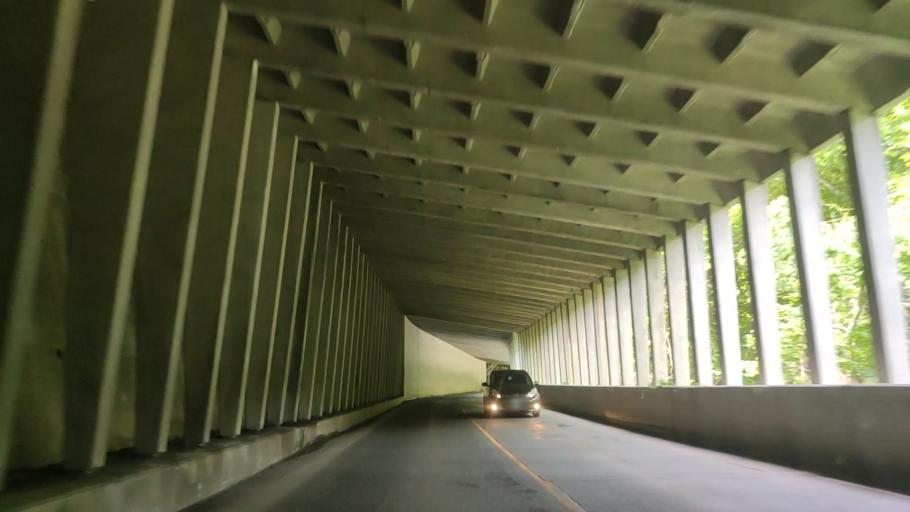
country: JP
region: Tochigi
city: Nikko
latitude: 36.8117
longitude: 139.3118
